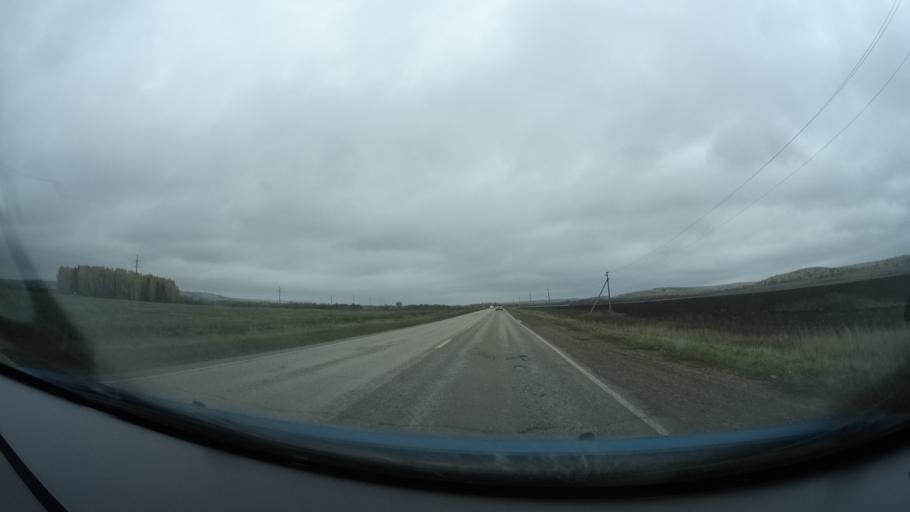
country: RU
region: Perm
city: Barda
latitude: 57.0665
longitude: 55.5423
